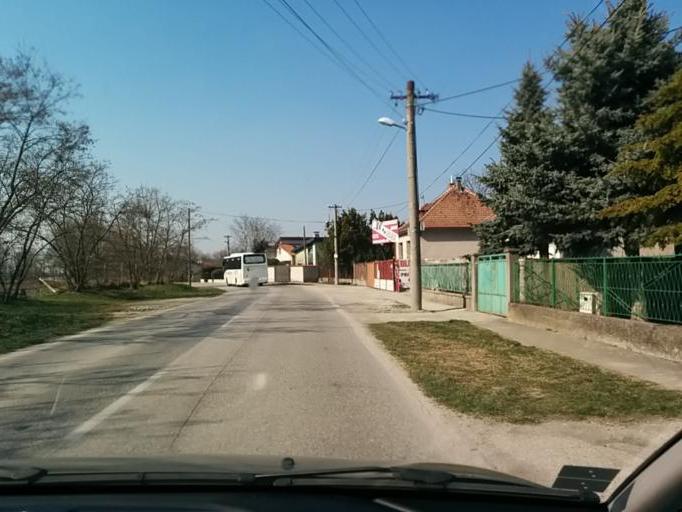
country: SK
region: Trnavsky
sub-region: Okres Galanta
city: Galanta
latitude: 48.2232
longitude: 17.7245
